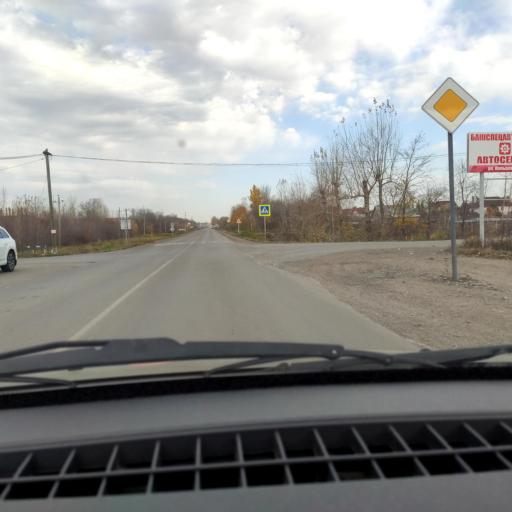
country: RU
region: Bashkortostan
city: Ufa
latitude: 54.6223
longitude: 55.9091
